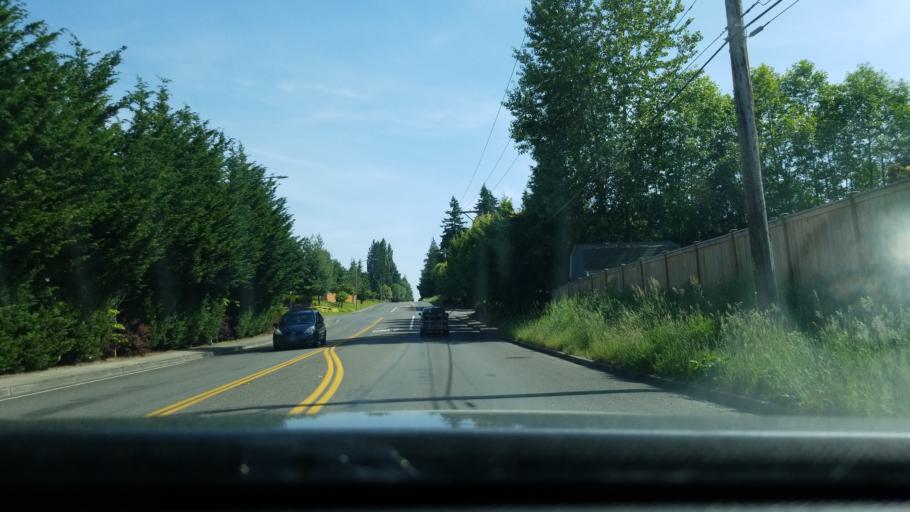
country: US
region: Washington
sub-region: Pierce County
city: Puyallup
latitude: 47.1689
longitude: -122.3043
